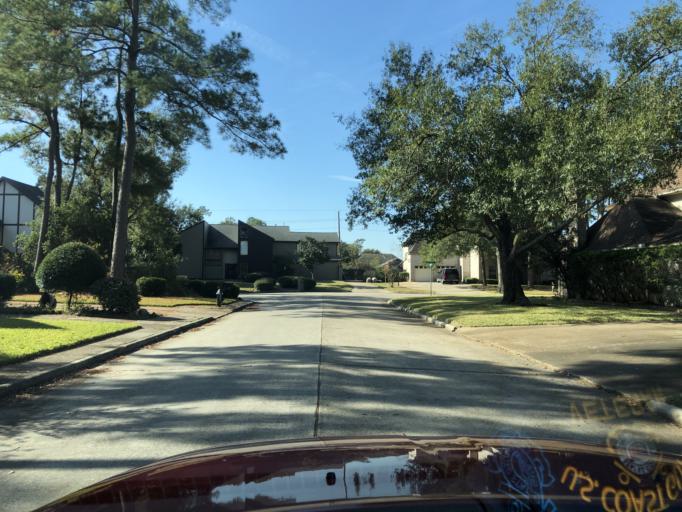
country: US
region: Texas
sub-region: Harris County
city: Tomball
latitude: 30.0283
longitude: -95.5545
